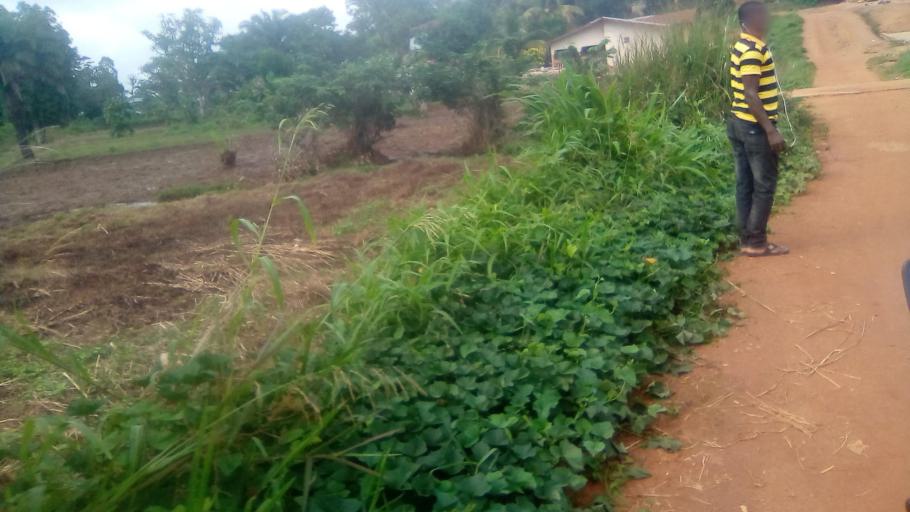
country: SL
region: Eastern Province
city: Kailahun
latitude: 8.2753
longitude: -10.5679
